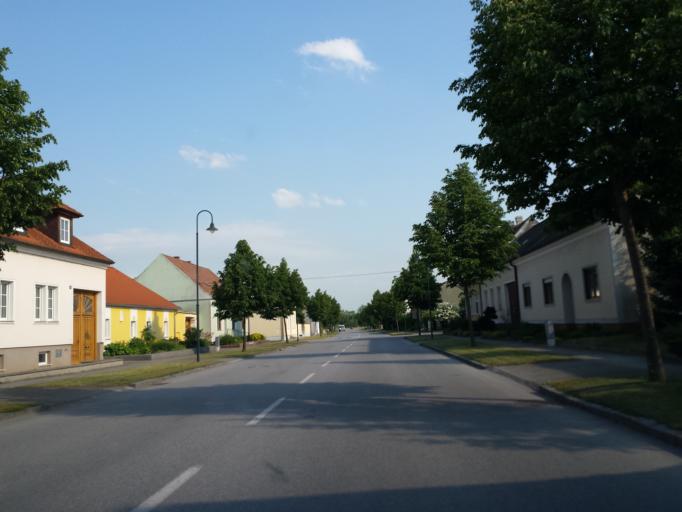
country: AT
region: Lower Austria
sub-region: Politischer Bezirk Ganserndorf
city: Marchegg
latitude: 48.3059
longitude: 16.8726
